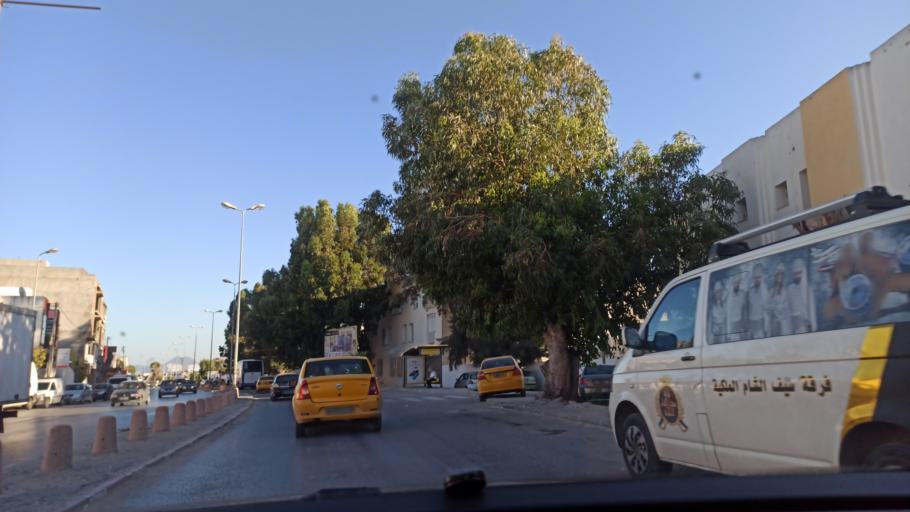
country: TN
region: Tunis
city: La Goulette
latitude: 36.8518
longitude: 10.2581
